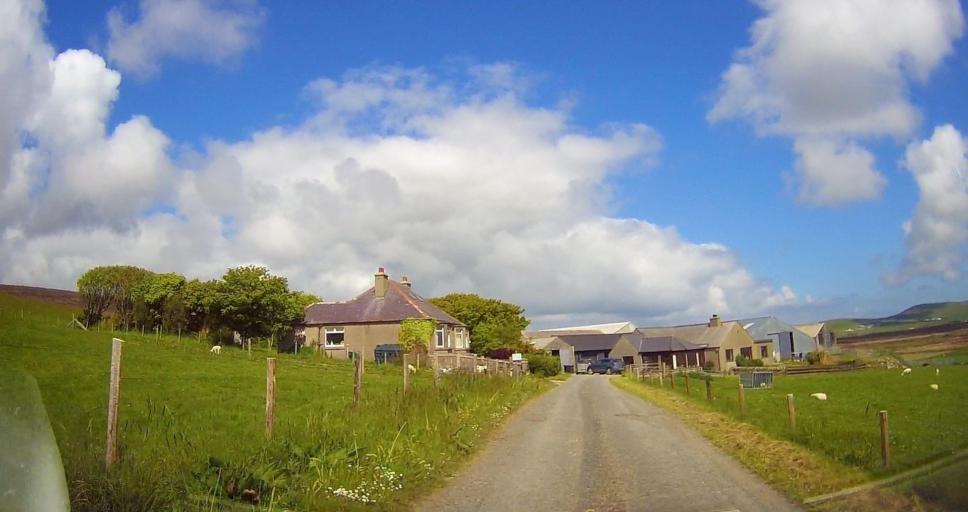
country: GB
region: Scotland
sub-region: Orkney Islands
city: Orkney
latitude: 59.0564
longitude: -3.1014
